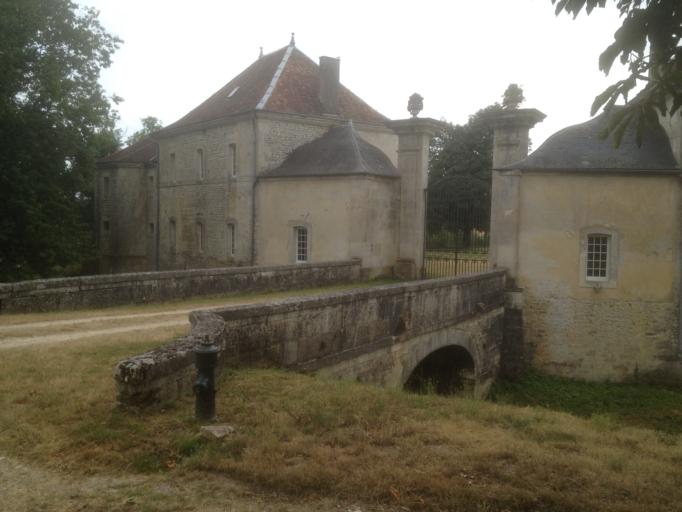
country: FR
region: Champagne-Ardenne
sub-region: Departement de la Haute-Marne
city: Joinville
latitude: 48.4614
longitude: 5.3120
